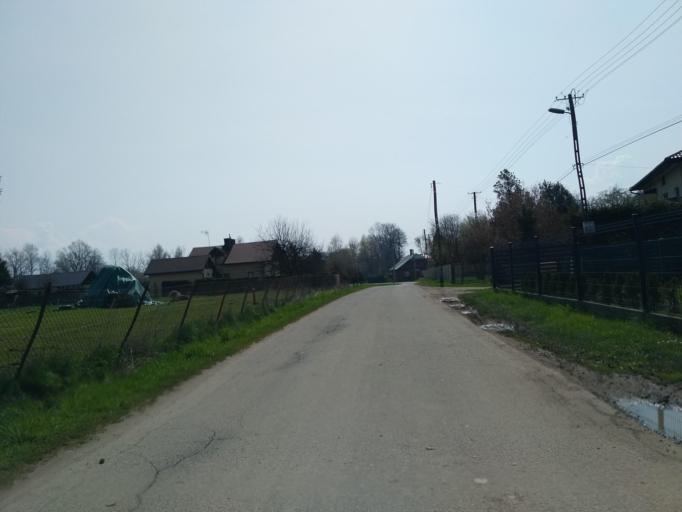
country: PL
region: Subcarpathian Voivodeship
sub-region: Powiat sanocki
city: Zarszyn
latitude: 49.6184
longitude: 22.0086
